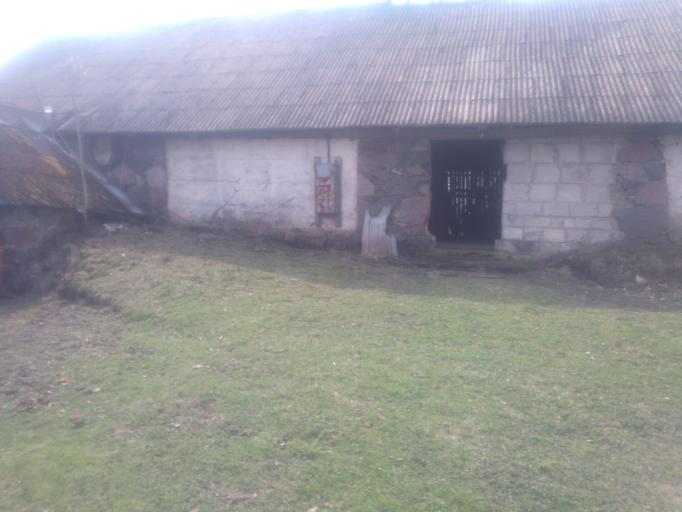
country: LV
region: Vecpiebalga
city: Vecpiebalga
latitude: 57.0240
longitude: 25.8521
